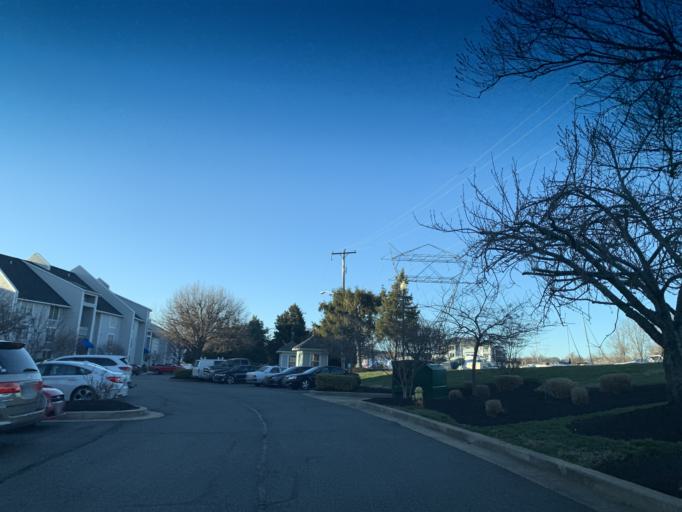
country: US
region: Maryland
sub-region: Cecil County
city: Perryville
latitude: 39.5586
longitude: -76.0795
